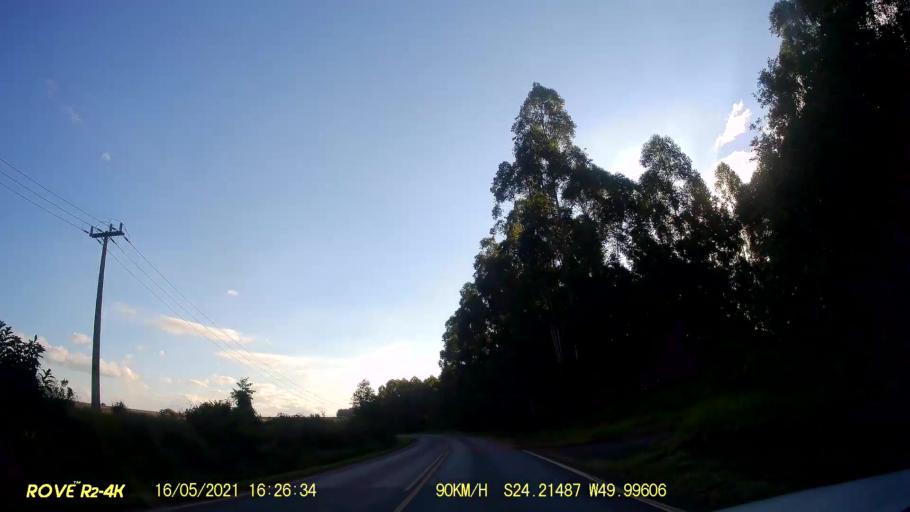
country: BR
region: Parana
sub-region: Jaguariaiva
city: Jaguariaiva
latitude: -24.2148
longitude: -49.9962
